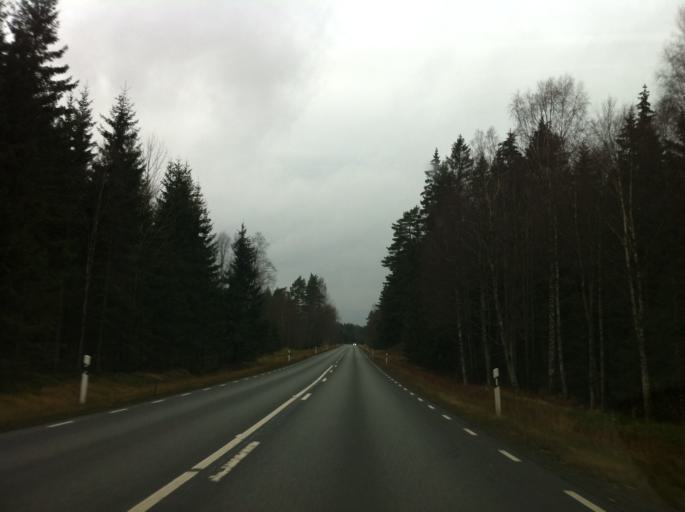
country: SE
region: Joenkoeping
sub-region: Savsjo Kommun
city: Saevsjoe
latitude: 57.3920
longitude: 14.7349
